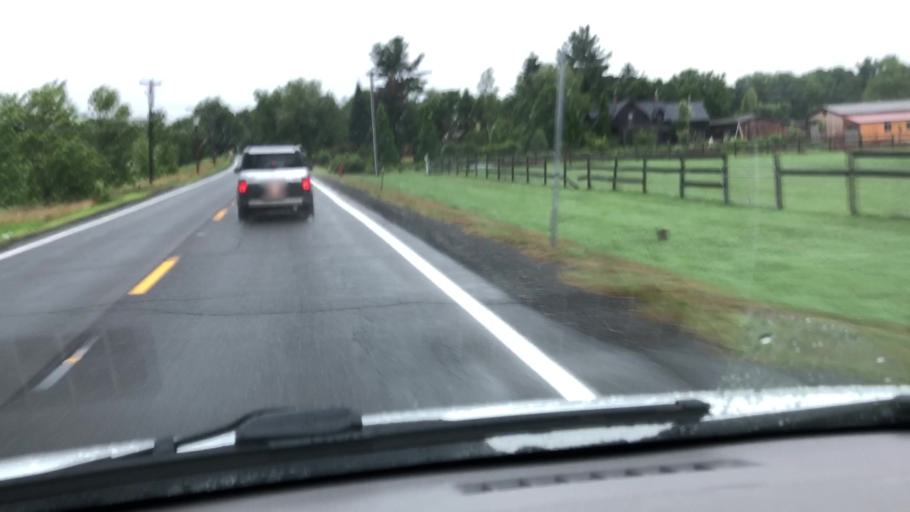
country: US
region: Massachusetts
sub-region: Hampshire County
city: Chesterfield
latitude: 42.3811
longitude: -72.9253
